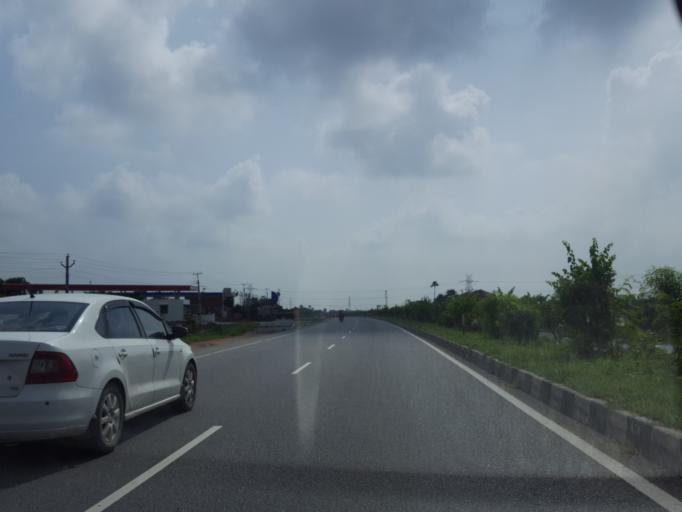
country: IN
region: Telangana
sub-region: Nalgonda
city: Gudur
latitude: 17.2649
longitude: 78.8324
